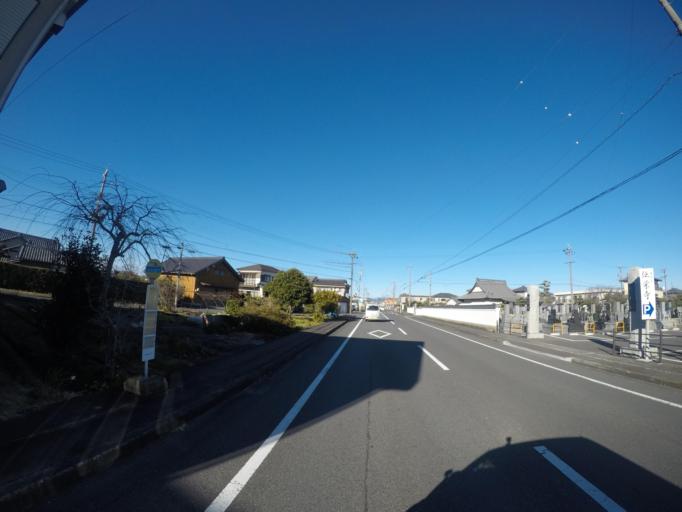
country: JP
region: Shizuoka
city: Fujieda
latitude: 34.8246
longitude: 138.2566
